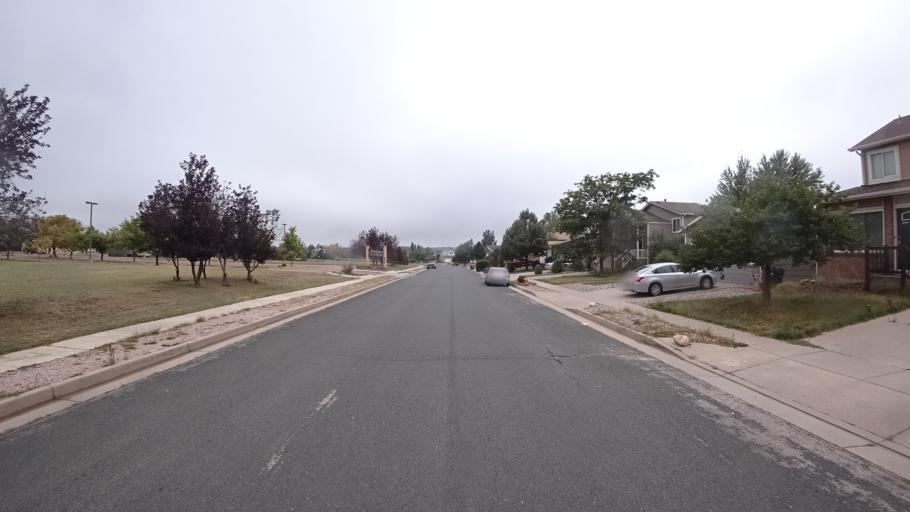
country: US
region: Colorado
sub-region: El Paso County
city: Cimarron Hills
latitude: 38.9281
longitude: -104.7282
